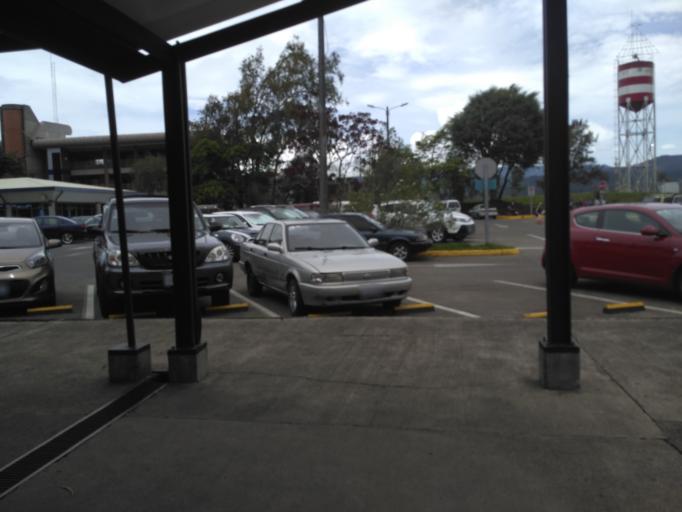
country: CR
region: Cartago
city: Cartago
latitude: 9.8559
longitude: -83.9136
